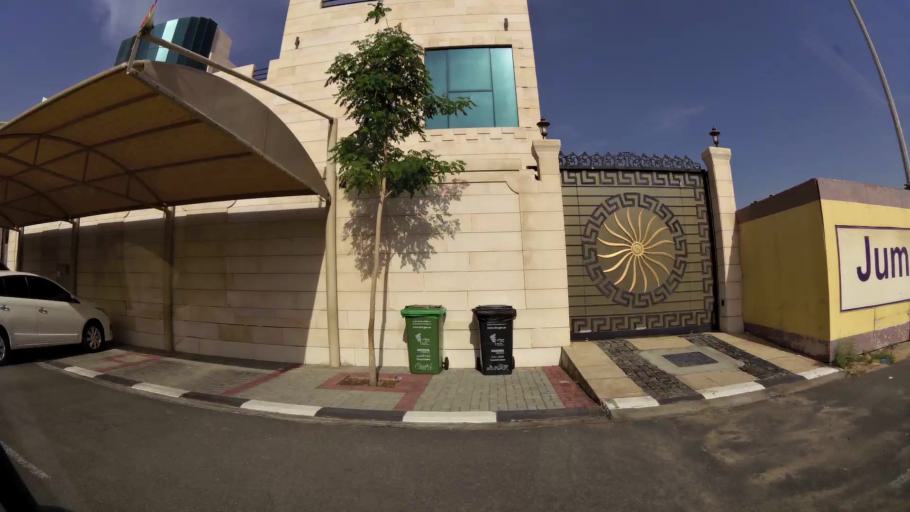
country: AE
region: Ash Shariqah
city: Sharjah
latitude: 25.2414
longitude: 55.4091
